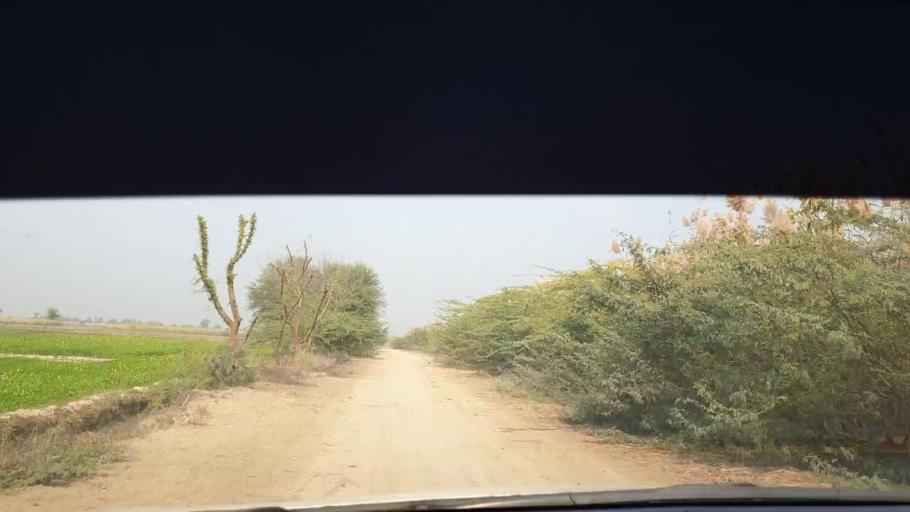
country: PK
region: Sindh
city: Berani
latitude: 25.8228
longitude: 68.8356
